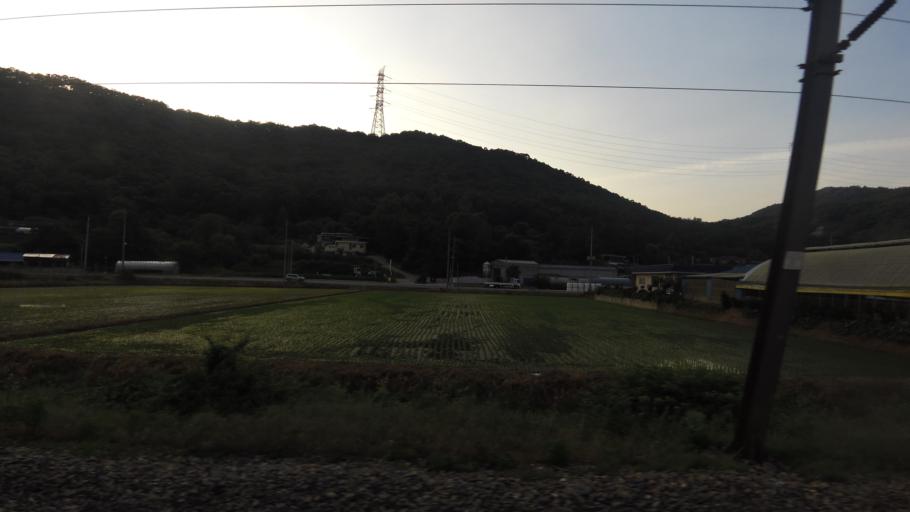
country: KR
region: Chungcheongnam-do
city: Cheonan
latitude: 36.6618
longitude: 127.2341
